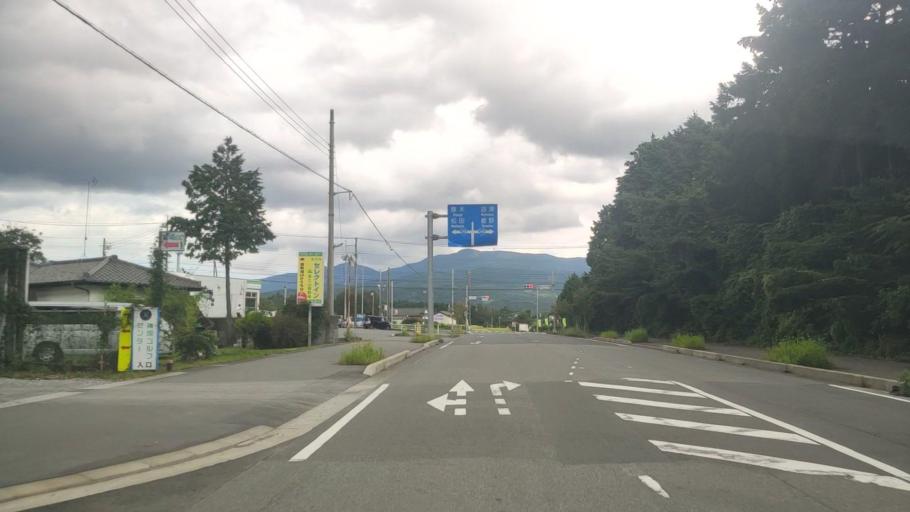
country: JP
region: Shizuoka
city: Gotemba
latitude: 35.2709
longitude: 138.9112
